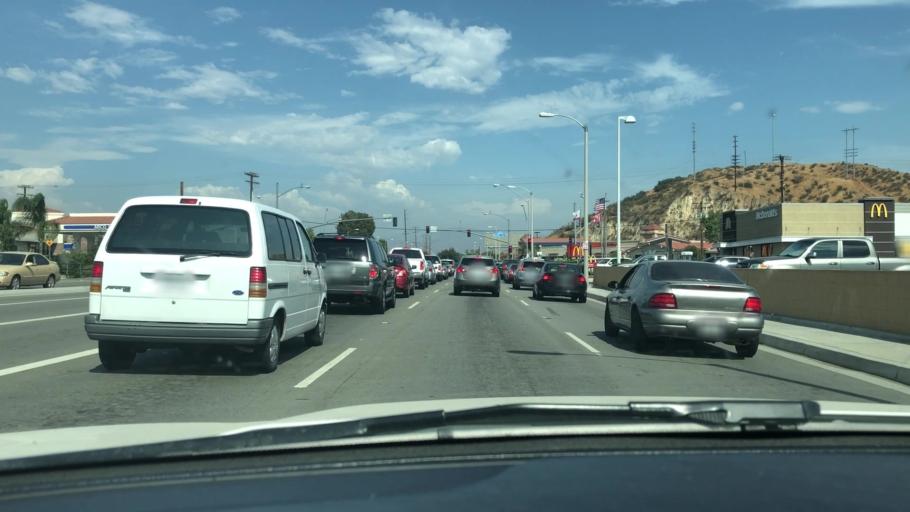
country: US
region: California
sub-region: Los Angeles County
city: Santa Clarita
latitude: 34.4229
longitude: -118.5425
